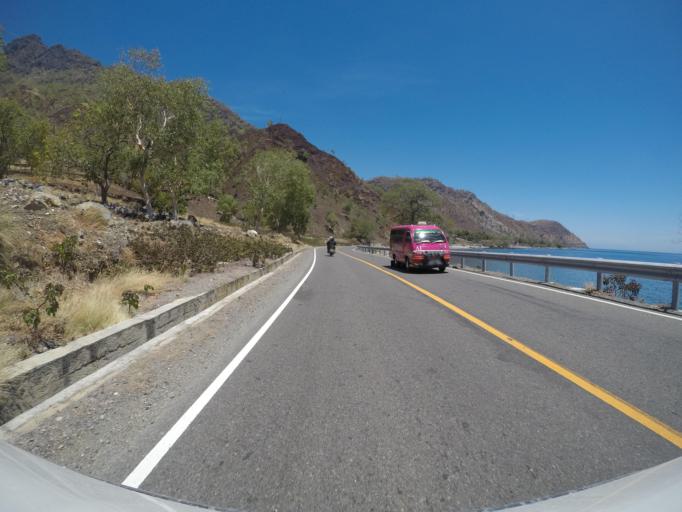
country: TL
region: Manatuto
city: Manatuto
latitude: -8.4797
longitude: 125.9270
